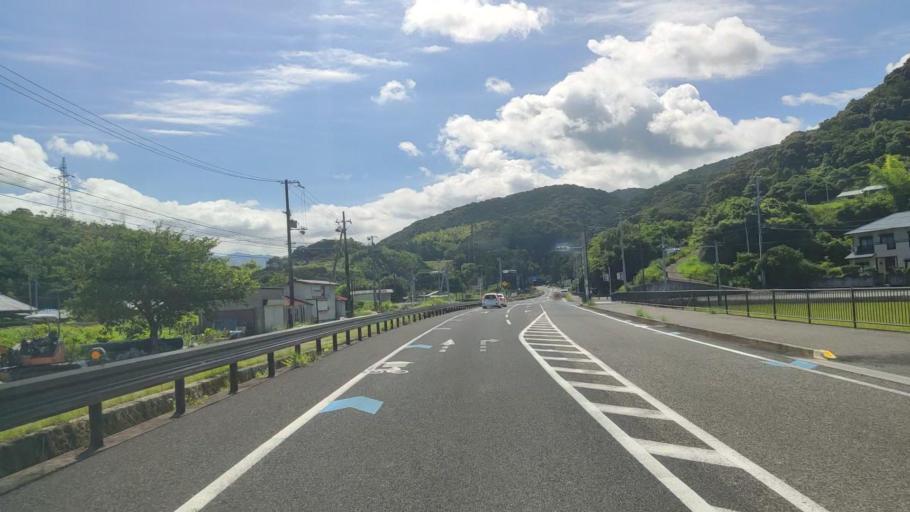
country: JP
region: Wakayama
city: Shingu
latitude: 33.7404
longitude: 136.0006
